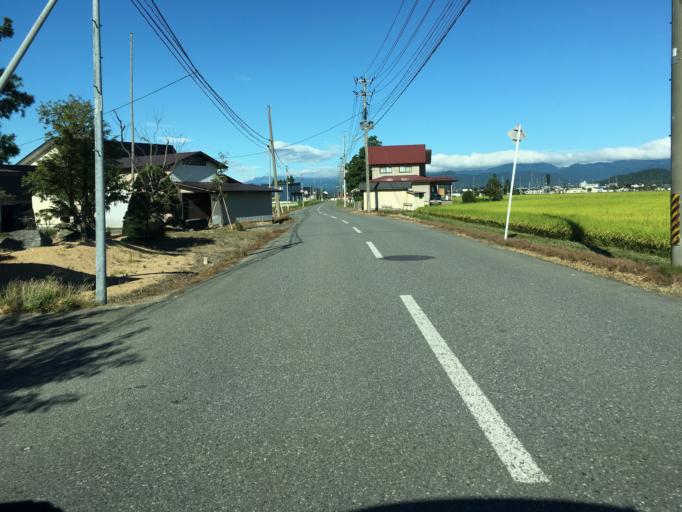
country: JP
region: Yamagata
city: Yonezawa
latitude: 37.9462
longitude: 140.1016
